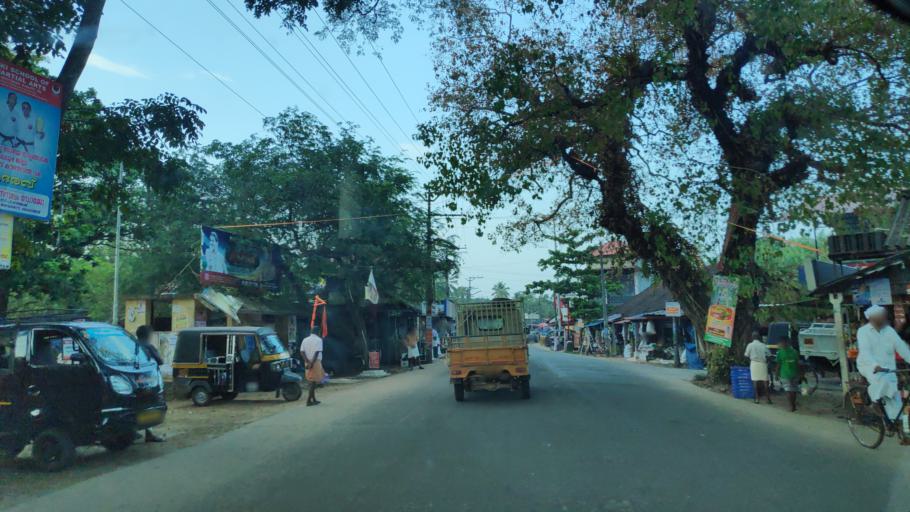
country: IN
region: Kerala
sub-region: Alappuzha
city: Shertallai
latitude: 9.6414
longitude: 76.3705
